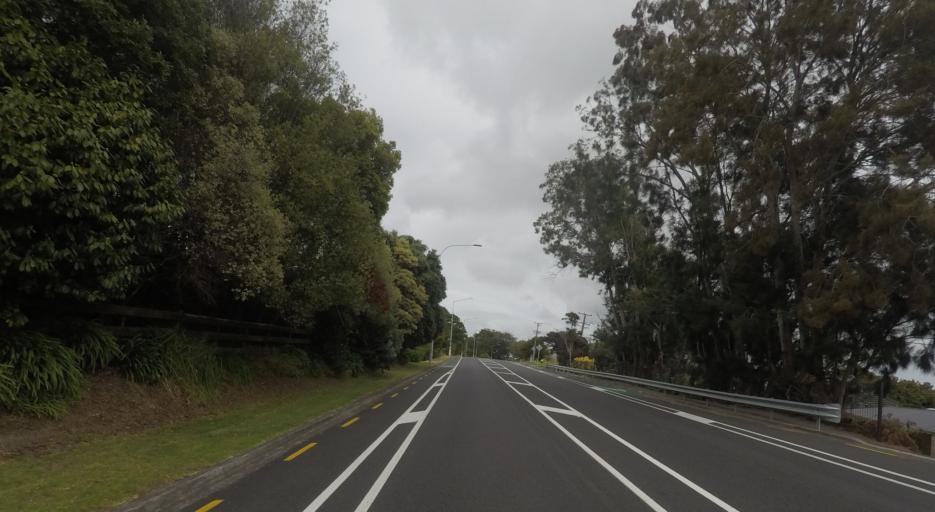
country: NZ
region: Auckland
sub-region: Auckland
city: North Shore
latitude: -36.7723
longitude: 174.6936
